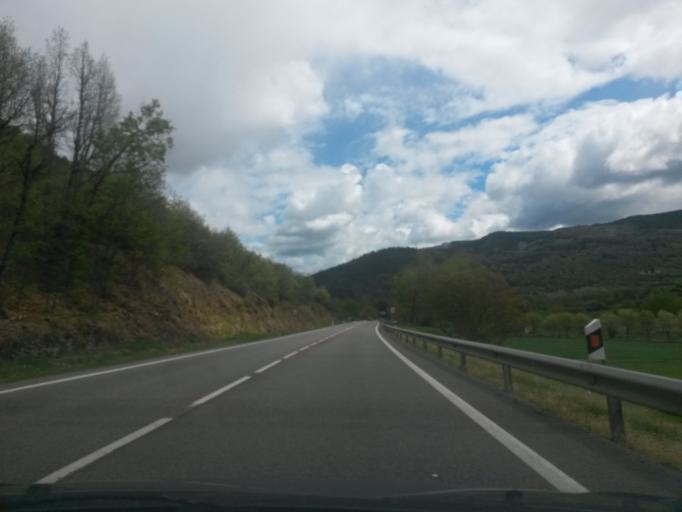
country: ES
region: Catalonia
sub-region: Provincia de Lleida
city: Alas i Cerc
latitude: 42.3579
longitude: 1.5010
